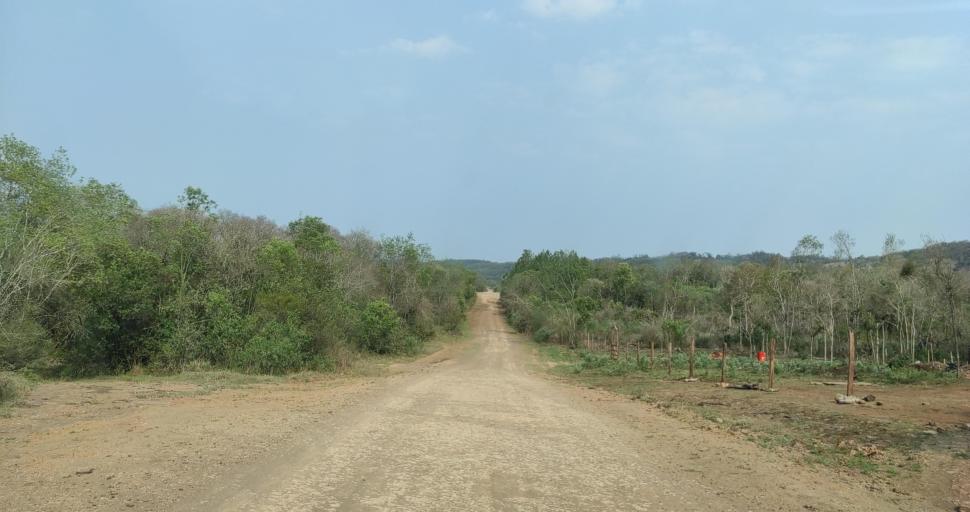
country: AR
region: Misiones
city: Cerro Azul
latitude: -27.6014
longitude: -55.5729
